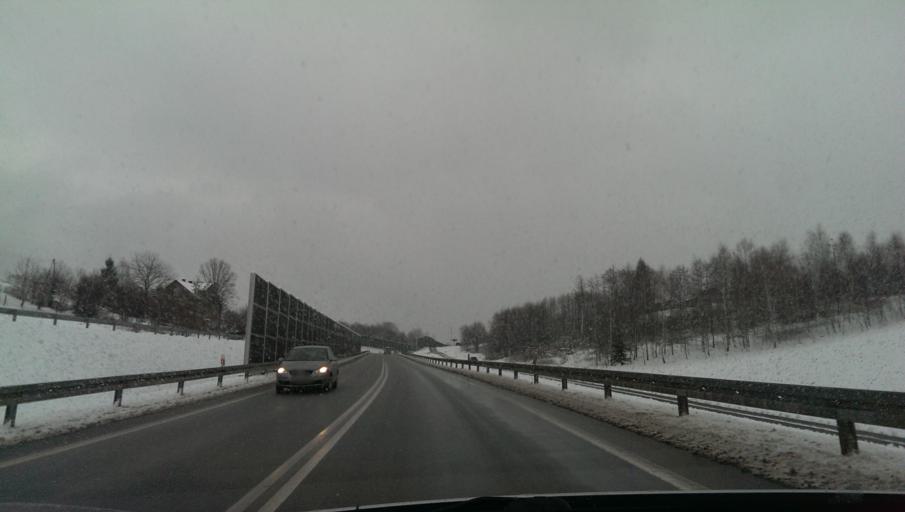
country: PL
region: Subcarpathian Voivodeship
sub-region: Powiat brzozowski
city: Brzozow
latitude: 49.6897
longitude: 22.0326
